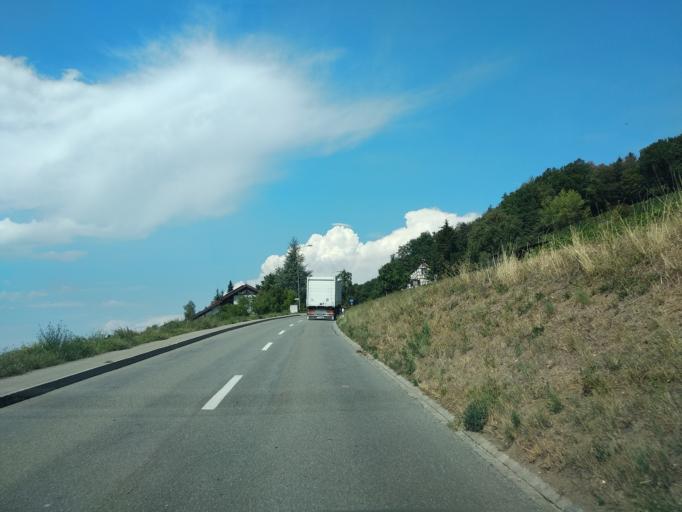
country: CH
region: Zurich
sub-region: Bezirk Winterthur
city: Sulz
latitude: 47.5969
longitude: 8.7810
